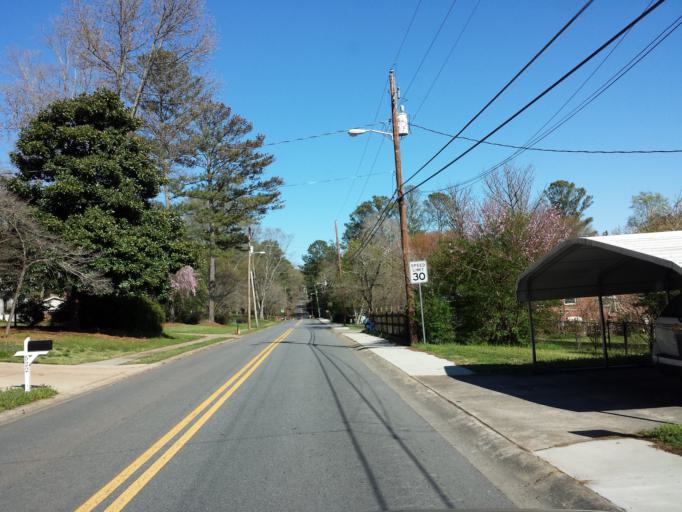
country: US
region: Georgia
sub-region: Cobb County
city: Marietta
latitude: 33.9594
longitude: -84.5678
